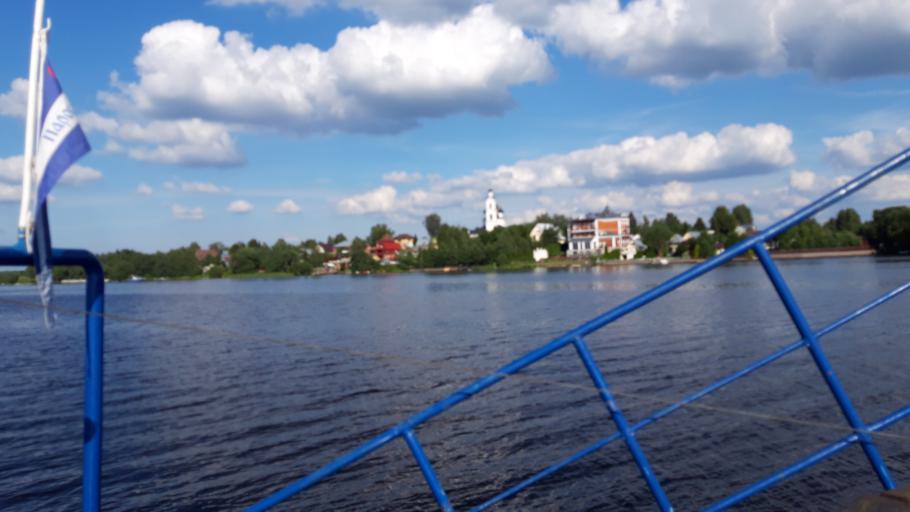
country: RU
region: Tverskaya
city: Zavidovo
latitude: 56.6327
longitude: 36.6067
